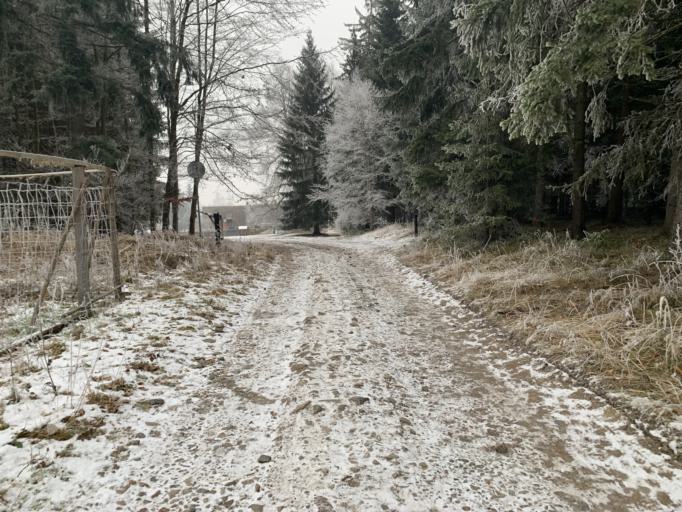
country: CZ
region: Central Bohemia
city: Rozmital pod Tremsinem
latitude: 49.5855
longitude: 13.8357
